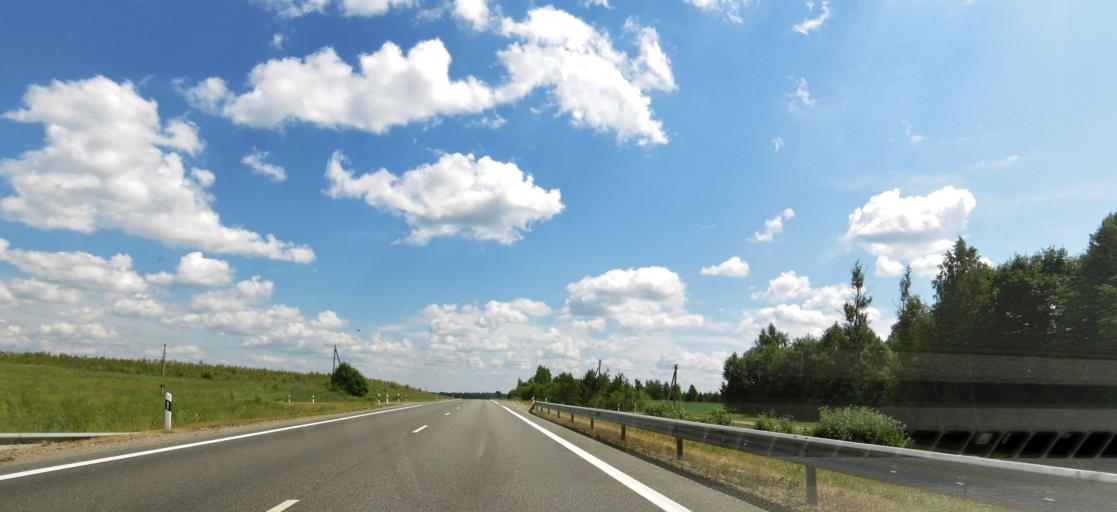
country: LT
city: Skaidiskes
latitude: 54.5658
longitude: 25.6405
